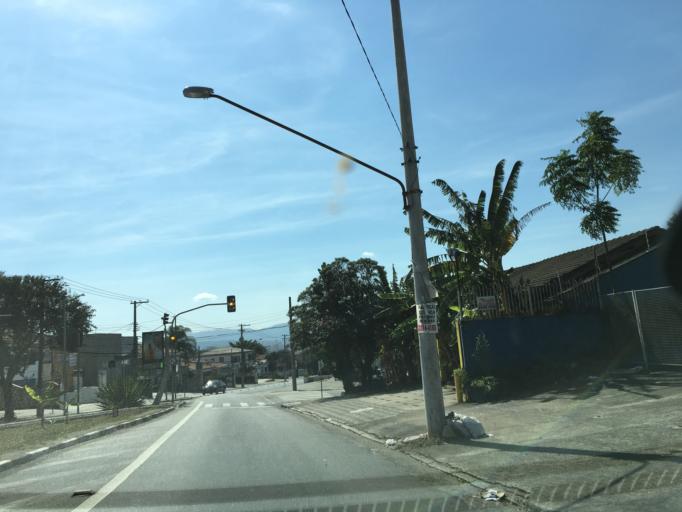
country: BR
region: Sao Paulo
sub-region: Sao Paulo
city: Sao Paulo
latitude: -23.5315
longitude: -46.7120
